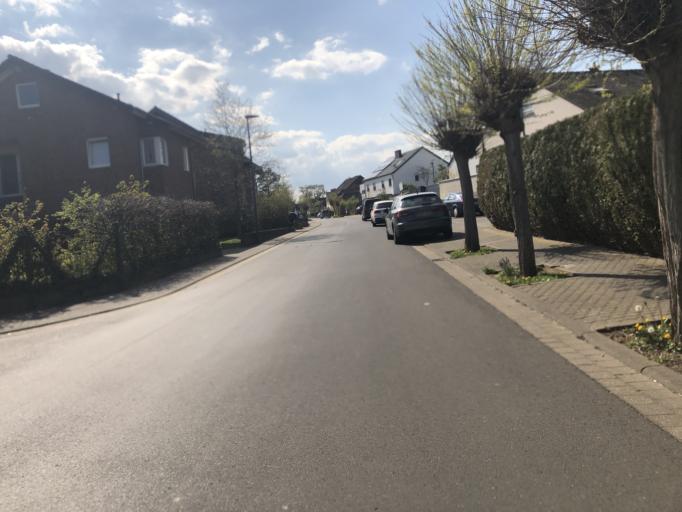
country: DE
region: North Rhine-Westphalia
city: Zulpich
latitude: 50.6931
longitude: 6.6585
